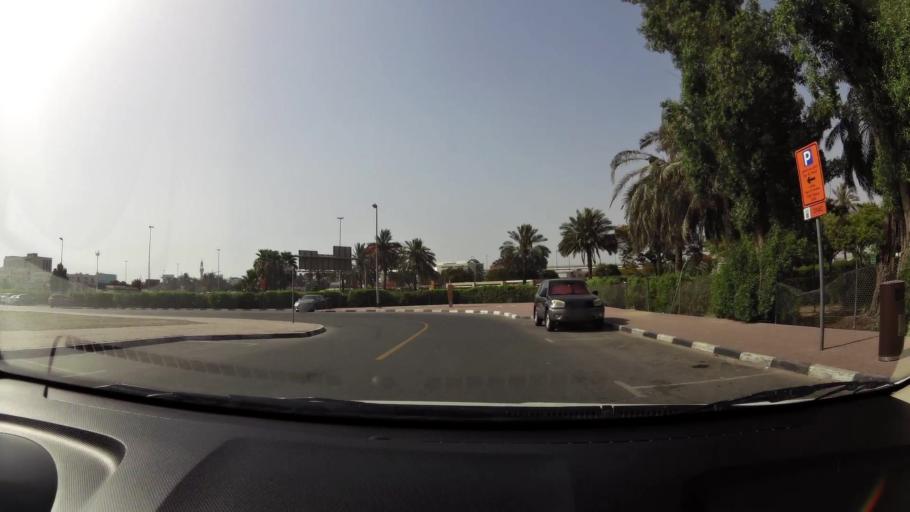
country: AE
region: Ash Shariqah
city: Sharjah
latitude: 25.2449
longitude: 55.3530
